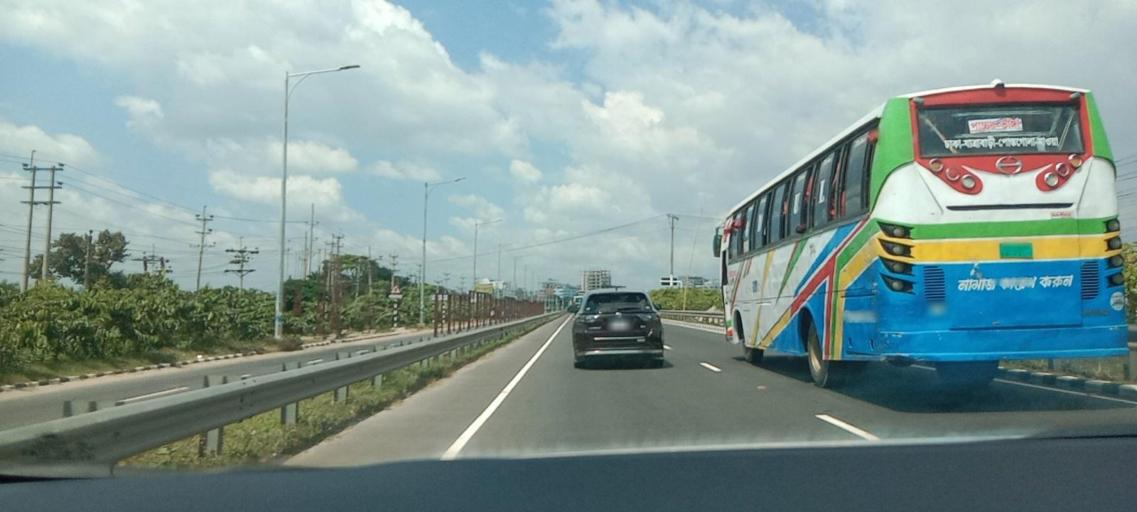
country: BD
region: Dhaka
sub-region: Dhaka
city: Dhaka
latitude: 23.6791
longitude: 90.4102
